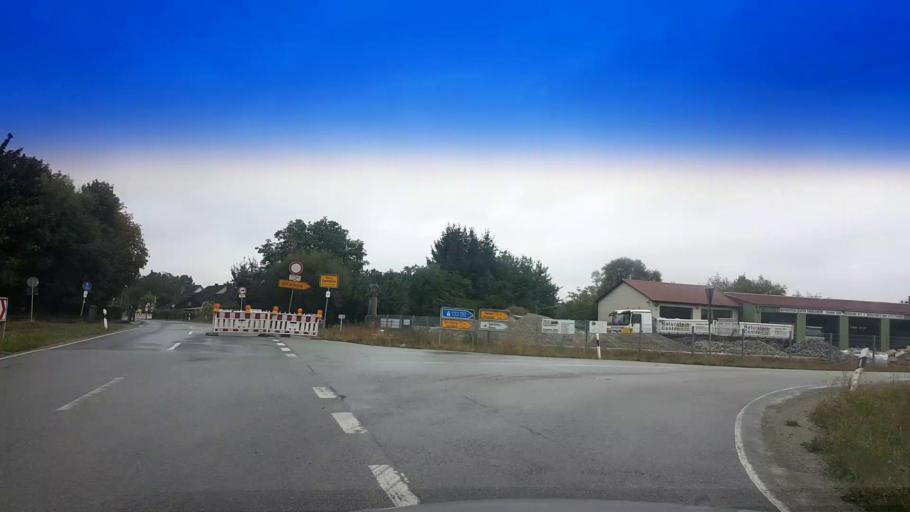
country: DE
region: Bavaria
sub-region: Upper Franconia
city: Eggolsheim
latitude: 49.7754
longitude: 11.0512
